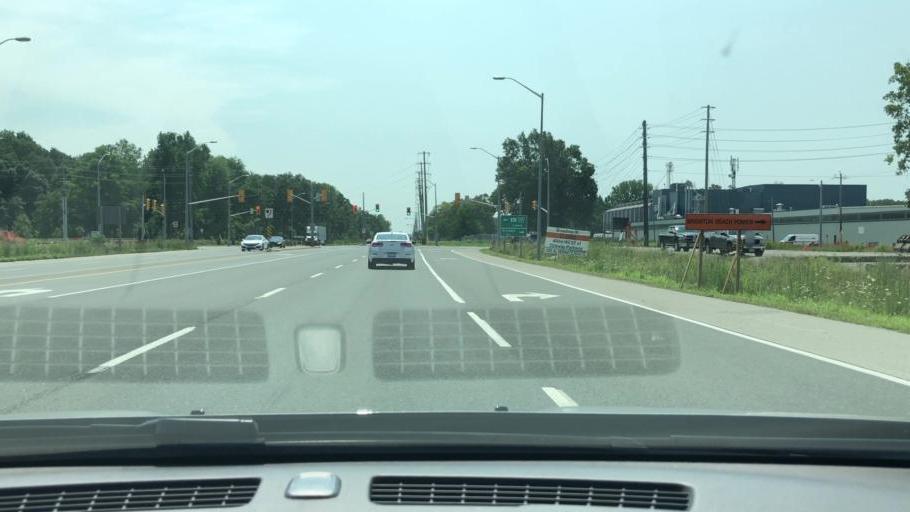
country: US
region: Michigan
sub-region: Wayne County
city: River Rouge
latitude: 42.2721
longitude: -83.0803
